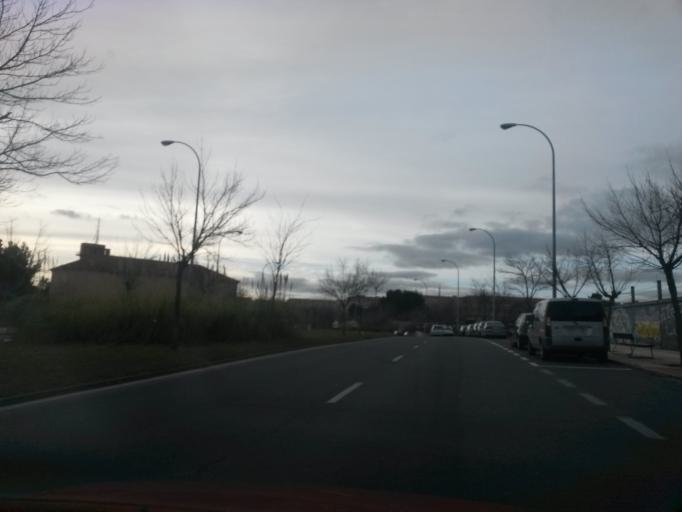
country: ES
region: Castille and Leon
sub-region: Provincia de Salamanca
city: Salamanca
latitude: 40.9797
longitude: -5.6586
